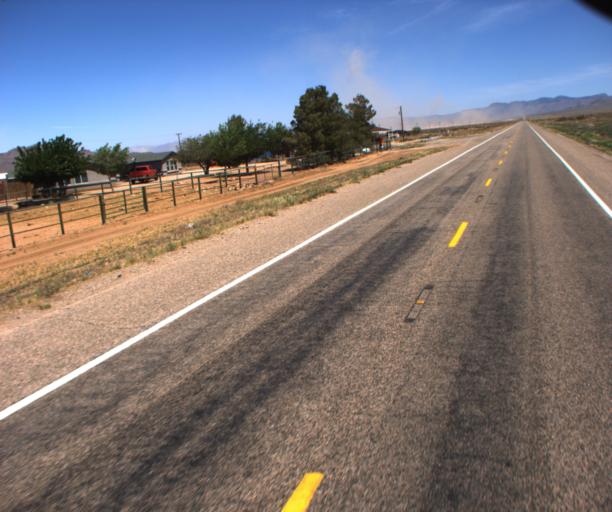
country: US
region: Arizona
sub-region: Mohave County
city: New Kingman-Butler
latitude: 35.3078
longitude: -113.9241
